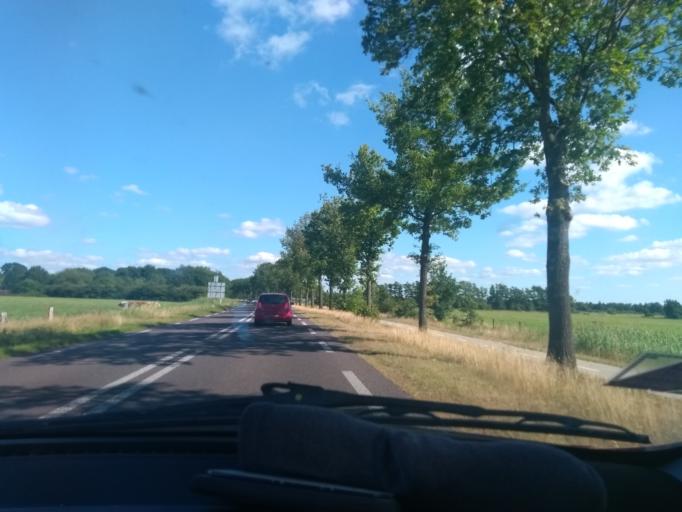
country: NL
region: Drenthe
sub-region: Gemeente Tynaarlo
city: Vries
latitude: 53.1098
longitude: 6.5203
